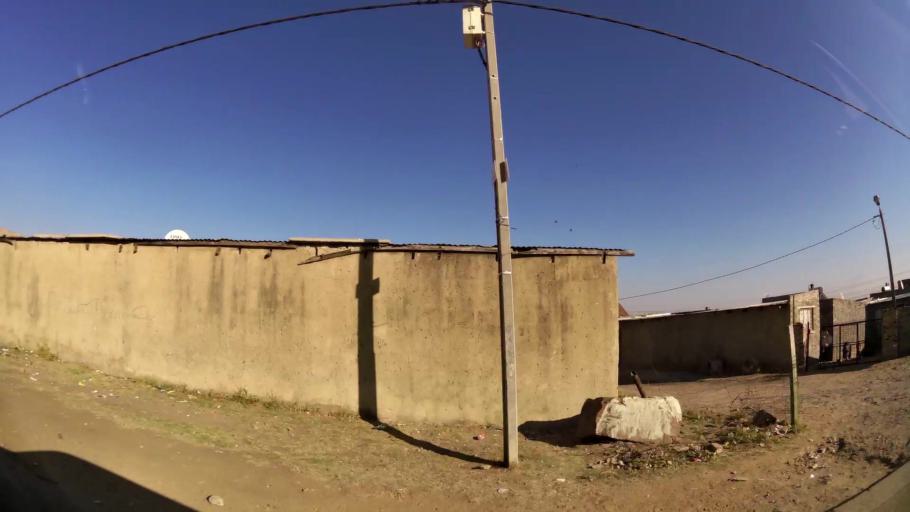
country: ZA
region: Gauteng
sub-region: City of Johannesburg Metropolitan Municipality
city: Modderfontein
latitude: -26.0411
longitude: 28.1576
